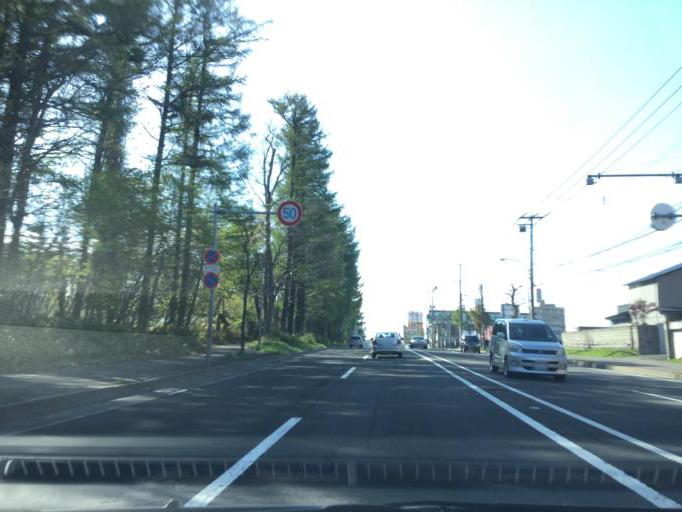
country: JP
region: Hokkaido
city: Sapporo
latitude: 43.0106
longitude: 141.4222
